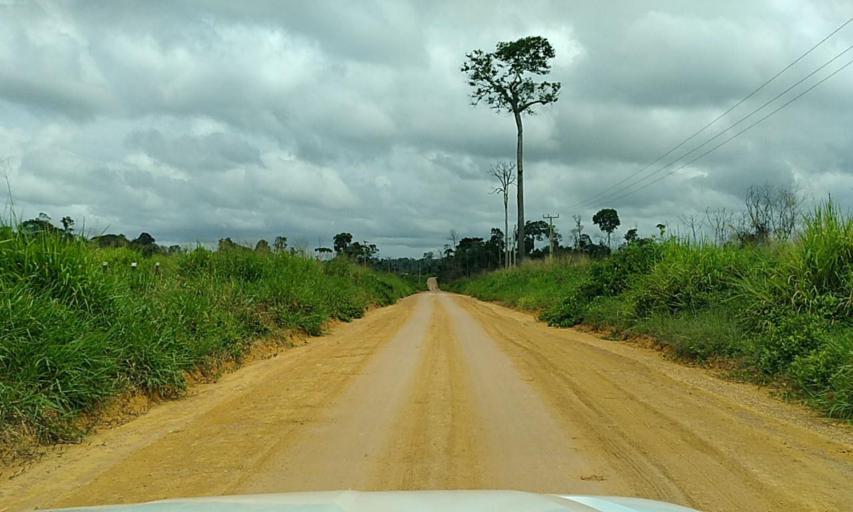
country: BR
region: Para
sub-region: Senador Jose Porfirio
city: Senador Jose Porfirio
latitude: -2.7698
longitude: -51.7817
